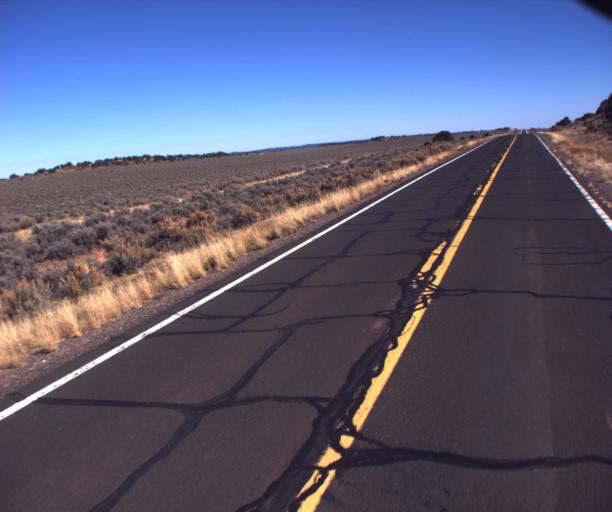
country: US
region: Arizona
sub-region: Navajo County
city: First Mesa
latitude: 35.7453
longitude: -110.0589
